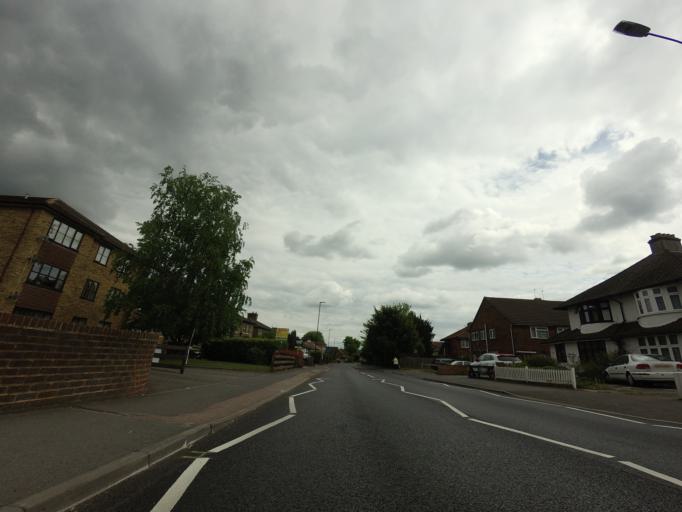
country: GB
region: England
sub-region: Greater London
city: Sidcup
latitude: 51.4201
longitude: 0.1148
